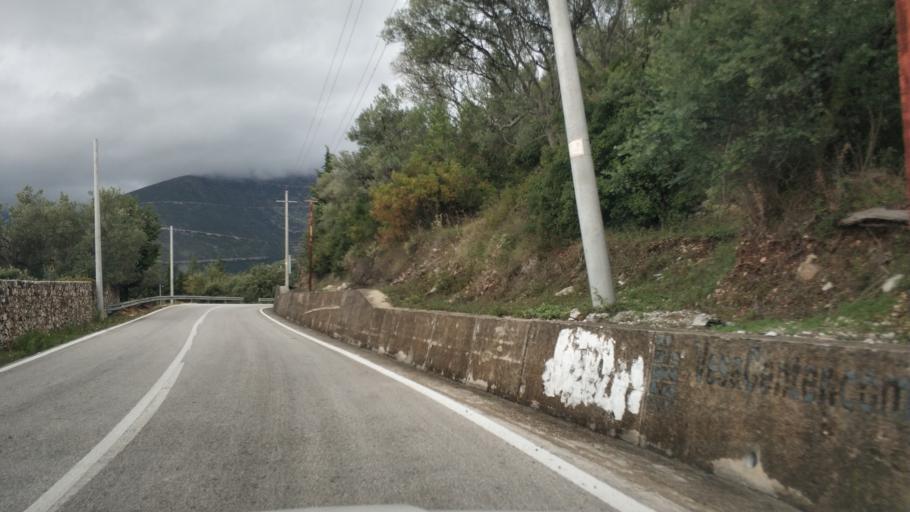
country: AL
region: Vlore
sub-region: Rrethi i Vlores
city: Vranisht
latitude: 40.1643
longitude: 19.6209
